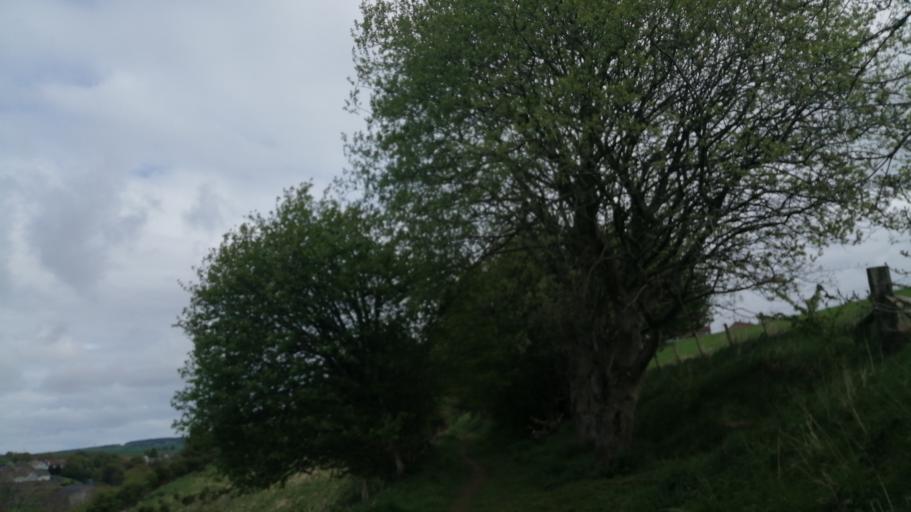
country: GB
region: Scotland
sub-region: Moray
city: Keith
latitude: 57.5342
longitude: -2.9606
